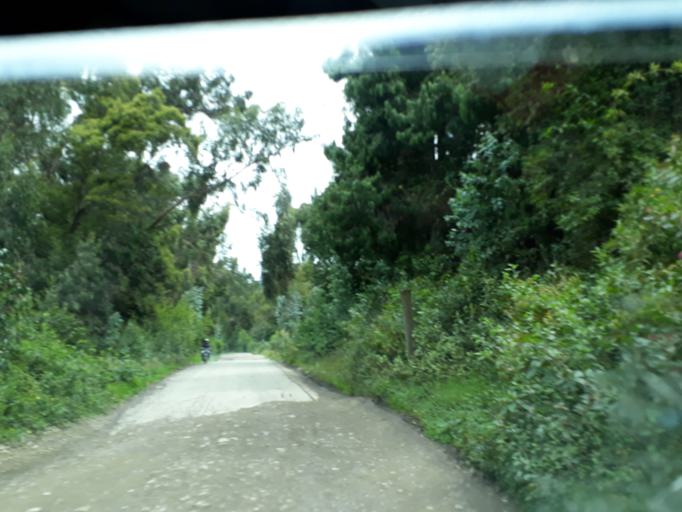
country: CO
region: Cundinamarca
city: Sutatausa
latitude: 5.1988
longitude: -73.8983
